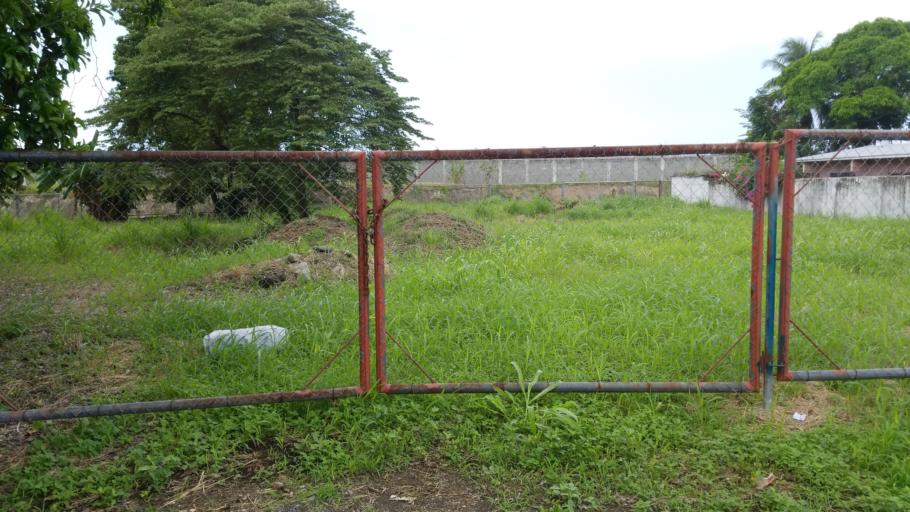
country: PA
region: Panama
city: San Miguelito
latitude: 9.0398
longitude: -79.4309
